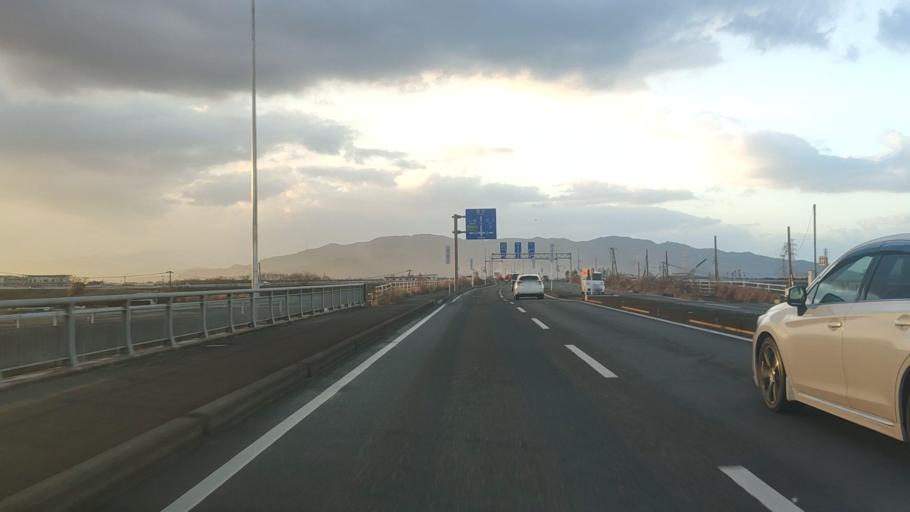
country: JP
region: Kumamoto
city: Kumamoto
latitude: 32.7400
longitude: 130.7047
